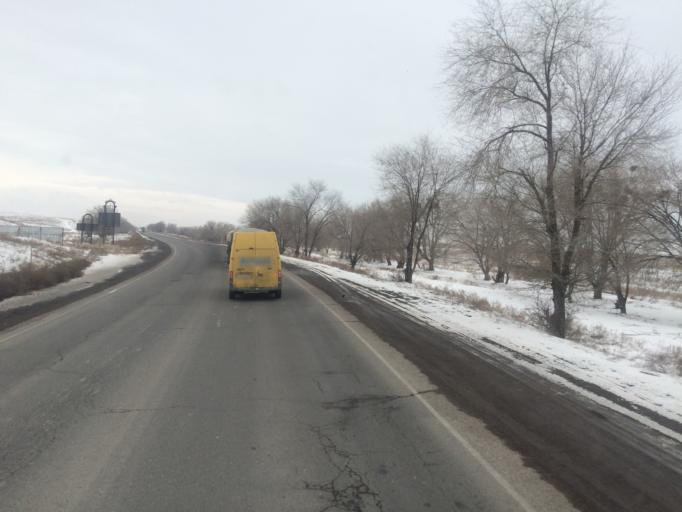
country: KG
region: Chuy
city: Bystrovka
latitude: 43.3299
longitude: 75.8292
